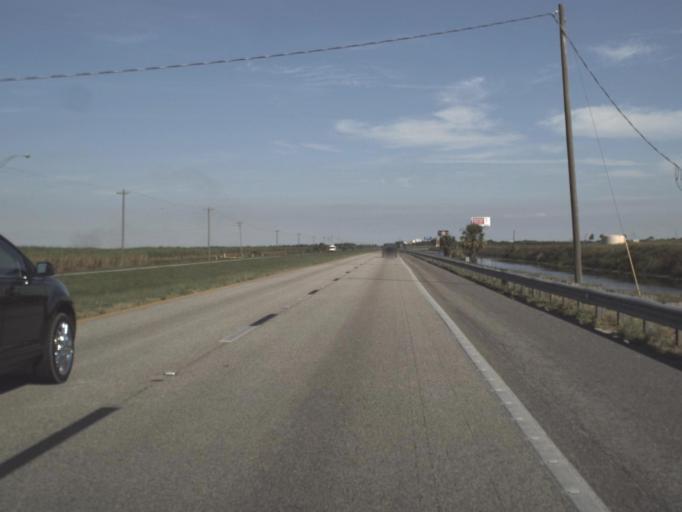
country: US
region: Florida
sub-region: Glades County
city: Moore Haven
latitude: 26.7536
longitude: -81.0562
